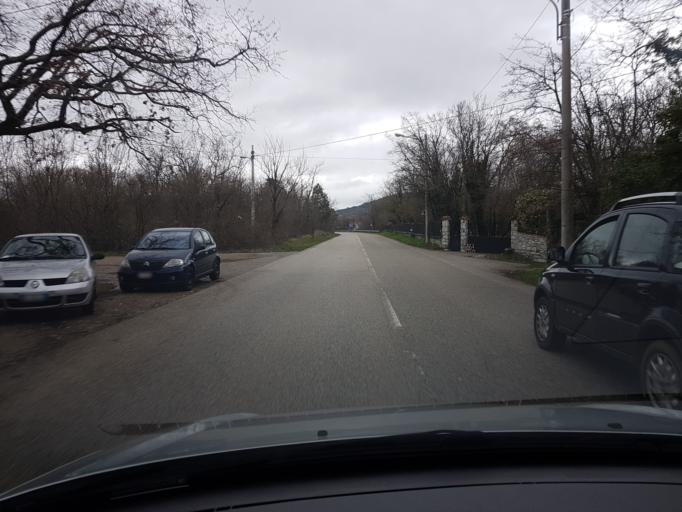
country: IT
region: Friuli Venezia Giulia
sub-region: Provincia di Trieste
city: Santa Croce
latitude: 45.7547
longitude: 13.7118
